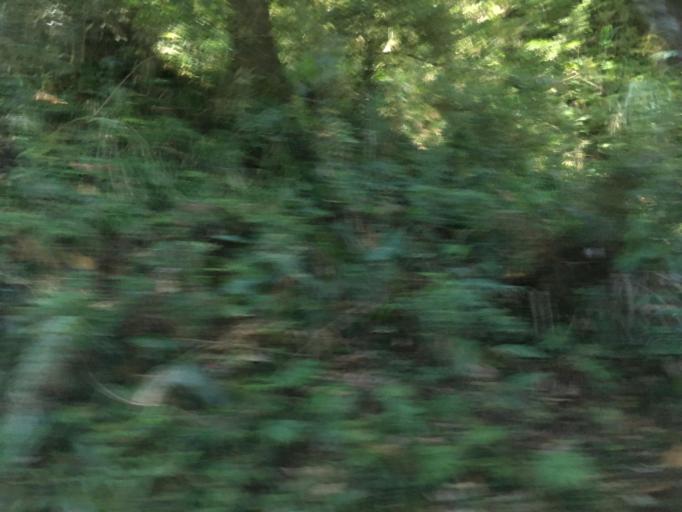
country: TW
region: Taiwan
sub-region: Yilan
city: Yilan
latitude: 24.6194
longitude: 121.4719
